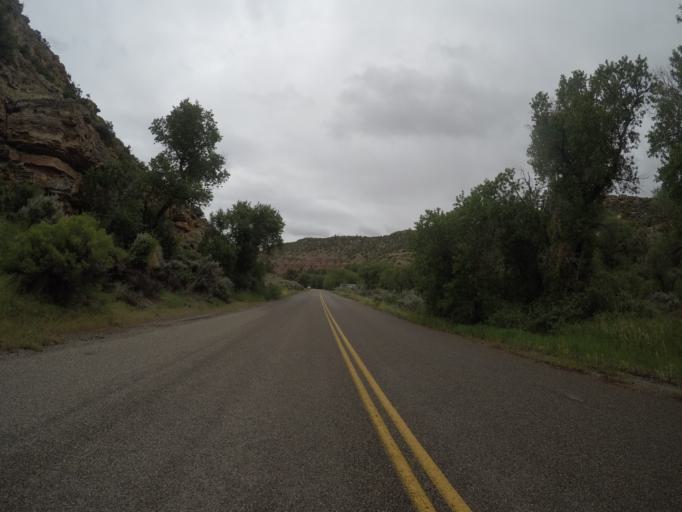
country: US
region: Wyoming
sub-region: Big Horn County
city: Lovell
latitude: 45.1060
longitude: -108.2259
